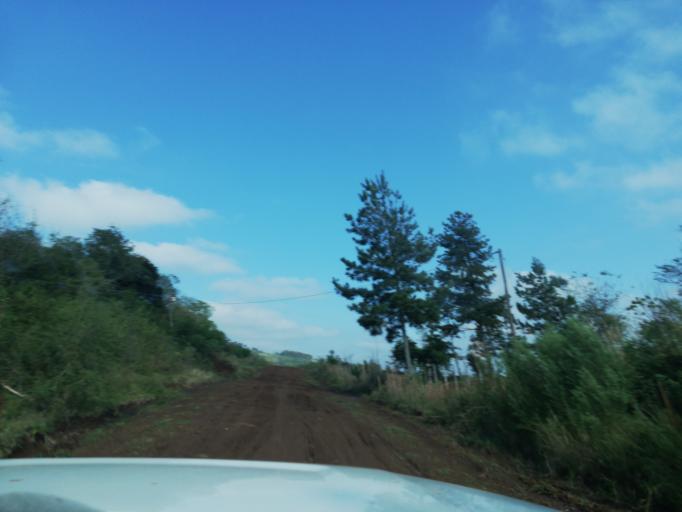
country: AR
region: Misiones
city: Cerro Azul
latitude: -27.5993
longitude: -55.5277
